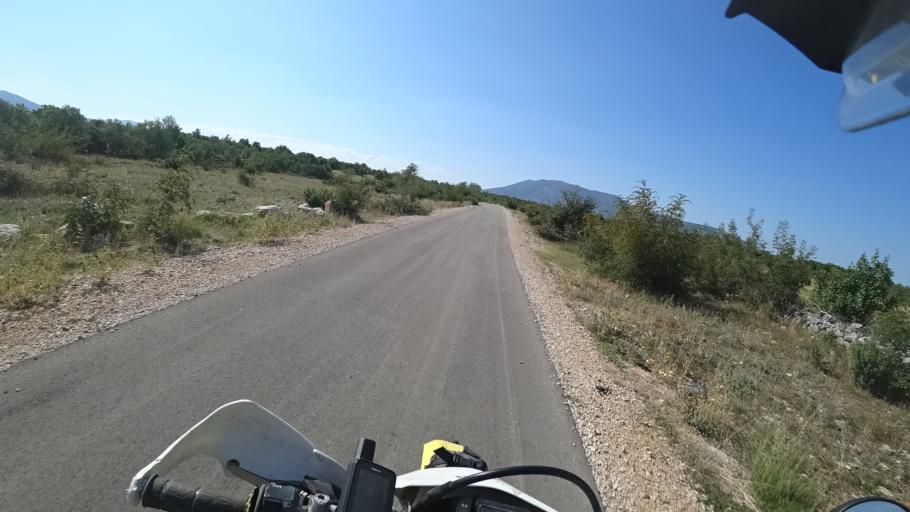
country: HR
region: Sibensko-Kniniska
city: Knin
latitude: 44.0057
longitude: 16.1934
